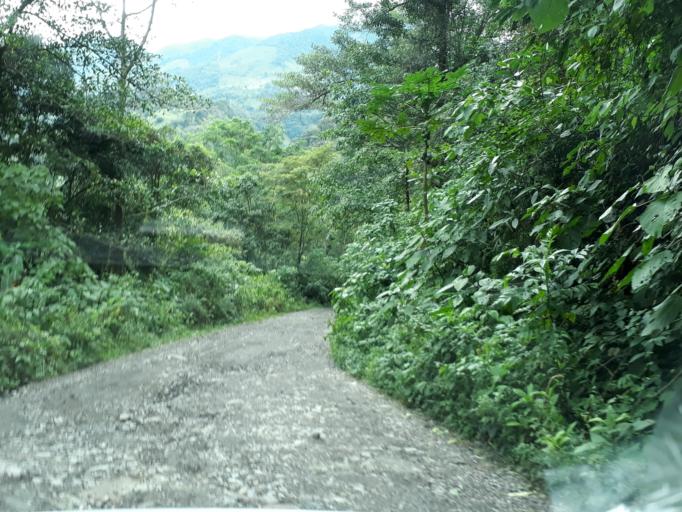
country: CO
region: Boyaca
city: Santa Maria
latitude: 4.7546
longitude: -73.3255
